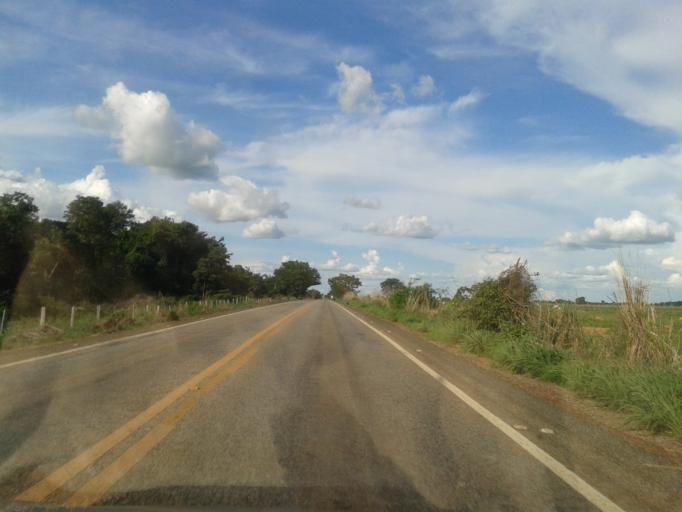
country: BR
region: Goias
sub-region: Mozarlandia
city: Mozarlandia
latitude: -14.5553
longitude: -50.4951
